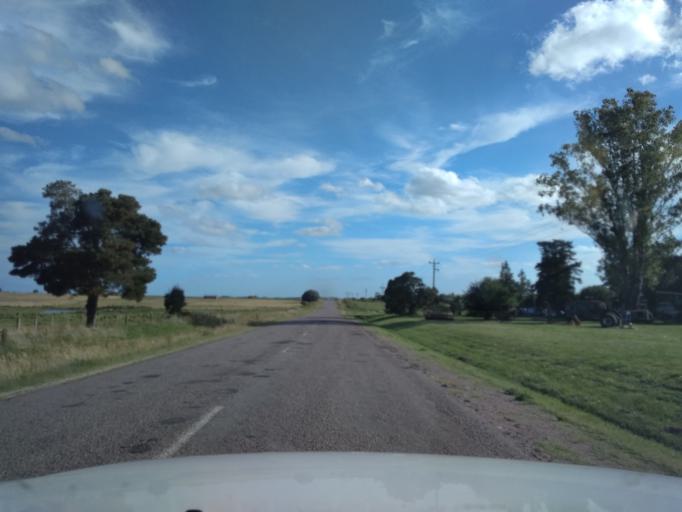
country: UY
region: Canelones
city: San Ramon
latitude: -34.2543
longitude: -55.9265
